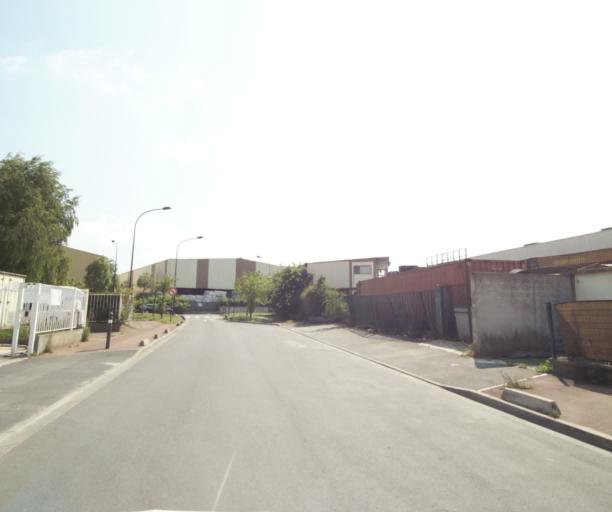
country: FR
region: Ile-de-France
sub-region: Departement des Yvelines
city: Sartrouville
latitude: 48.9494
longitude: 2.2115
